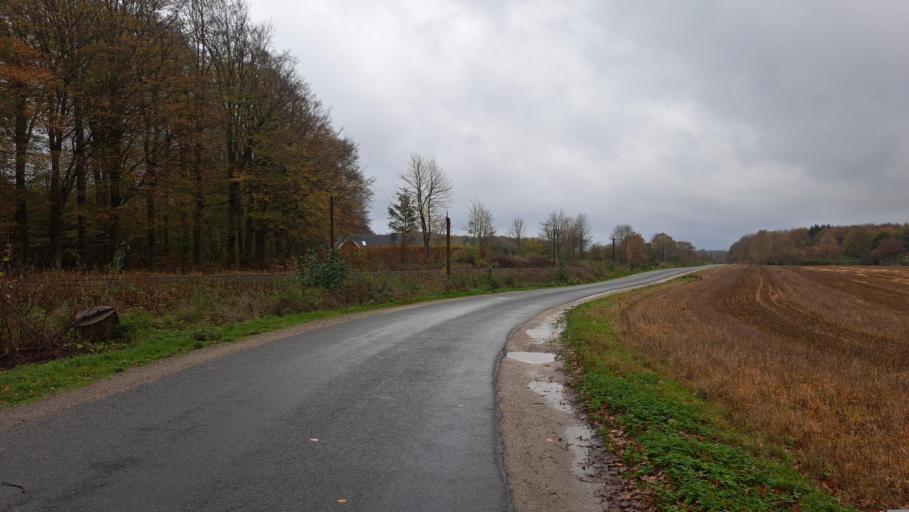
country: DK
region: Central Jutland
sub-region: Hedensted Kommune
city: Hedensted
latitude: 55.8216
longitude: 9.7213
